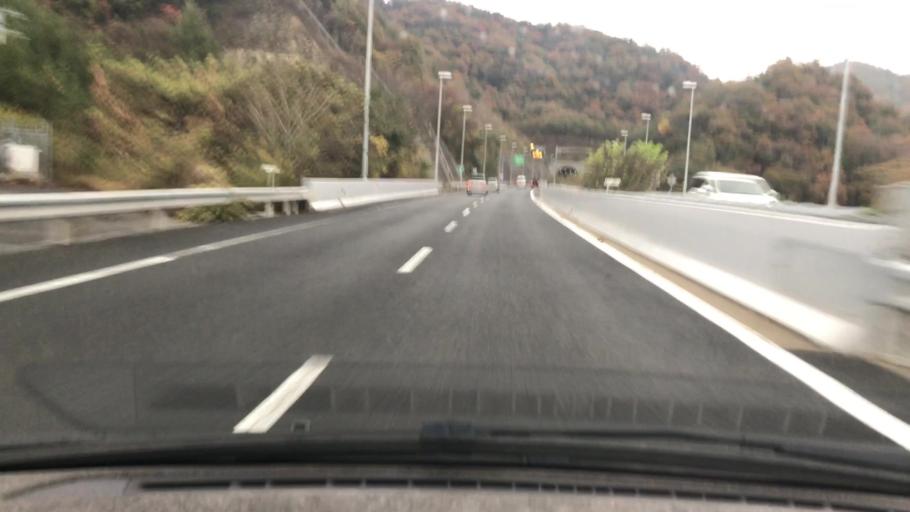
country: JP
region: Hyogo
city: Sandacho
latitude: 34.7976
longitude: 135.2296
